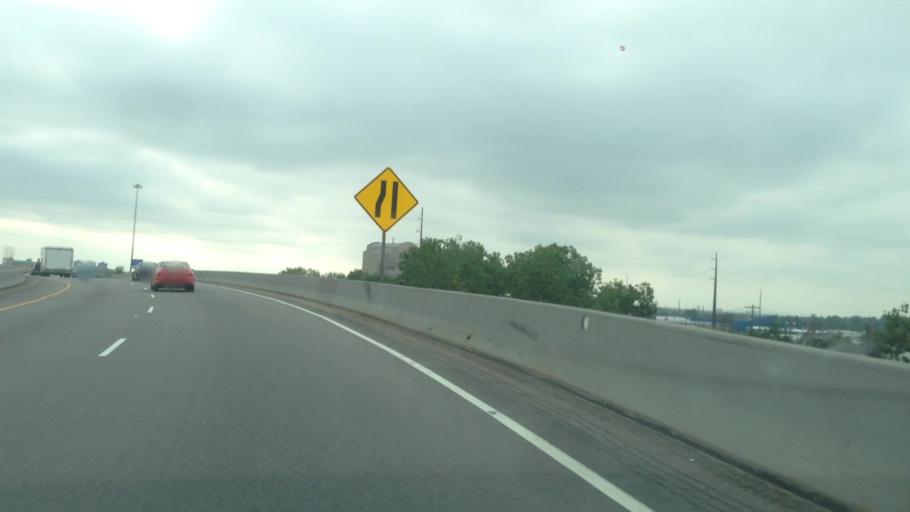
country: US
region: Colorado
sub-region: Denver County
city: Denver
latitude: 39.7241
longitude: -105.0145
